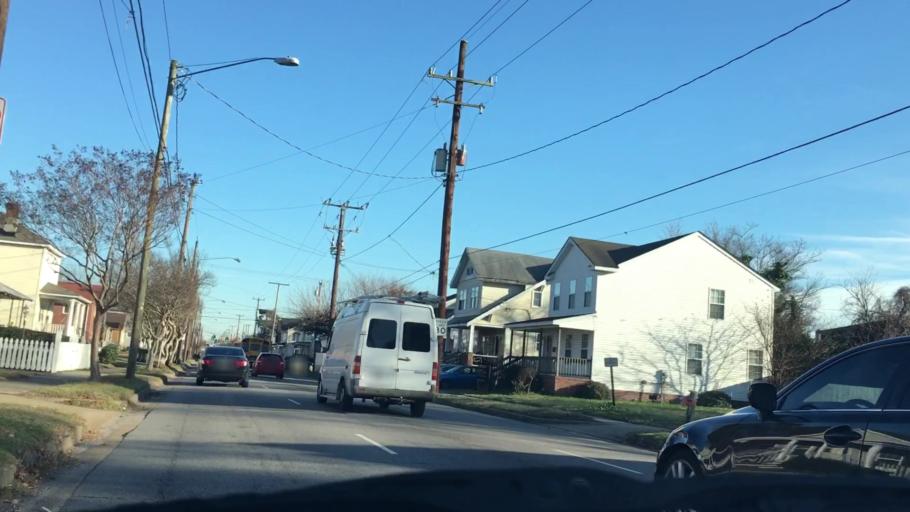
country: US
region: Virginia
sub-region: City of Norfolk
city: Norfolk
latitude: 36.8728
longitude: -76.2896
